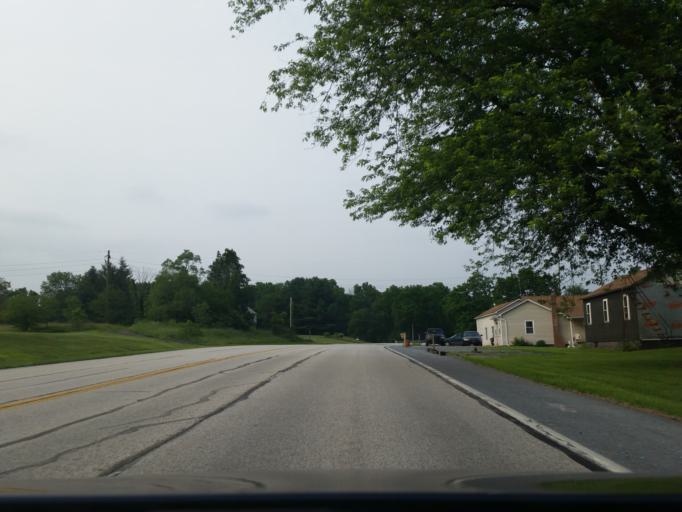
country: US
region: Pennsylvania
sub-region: Lebanon County
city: Jonestown
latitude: 40.4410
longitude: -76.5383
